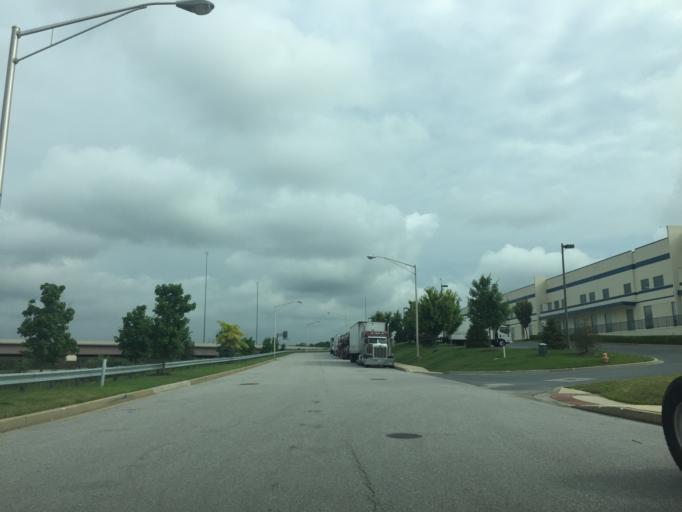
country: US
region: Maryland
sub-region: Baltimore County
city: Rosedale
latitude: 39.3160
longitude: -76.5324
